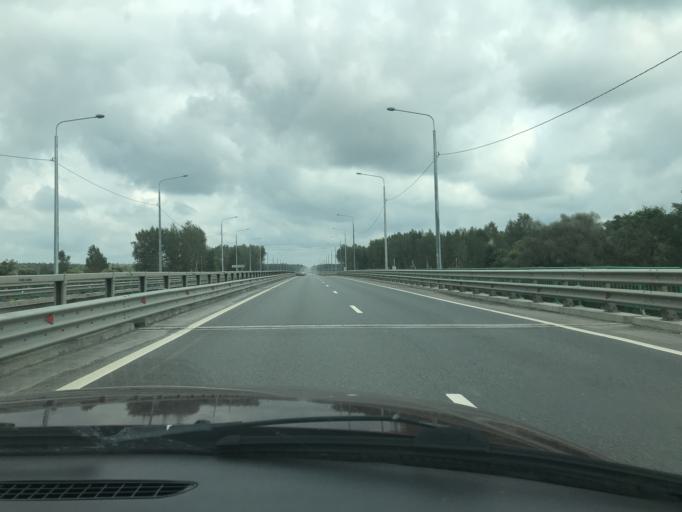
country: RU
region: Kaluga
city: Detchino
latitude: 54.7398
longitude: 36.1892
